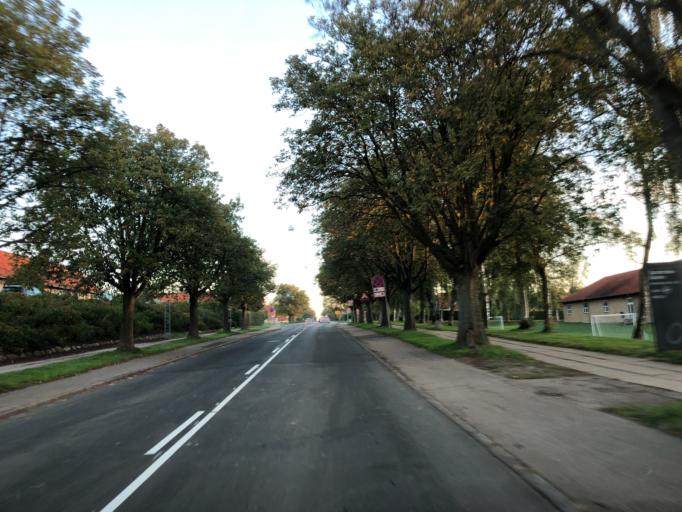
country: DK
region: South Denmark
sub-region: Sonderborg Kommune
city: Sonderborg
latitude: 54.9055
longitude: 9.8108
